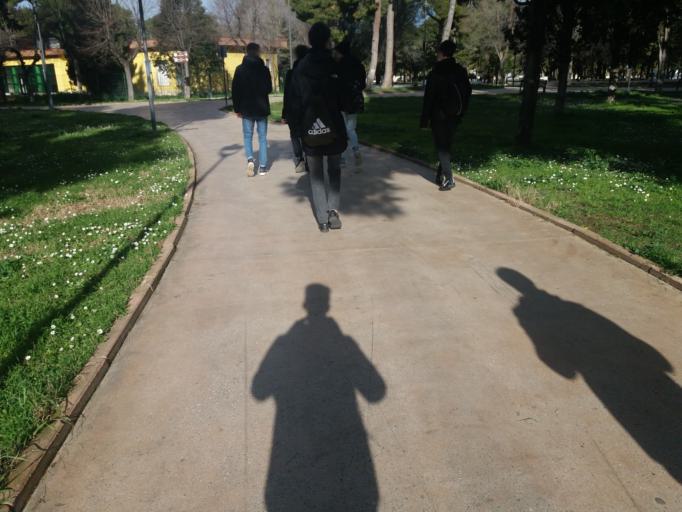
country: IT
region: Apulia
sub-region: Provincia di Barletta - Andria - Trani
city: Andria
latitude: 41.2310
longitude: 16.3070
